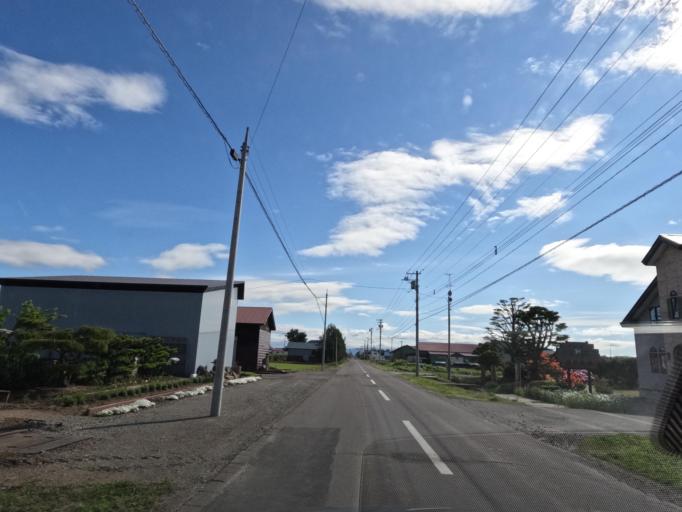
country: JP
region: Hokkaido
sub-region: Asahikawa-shi
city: Asahikawa
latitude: 43.7222
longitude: 142.5249
